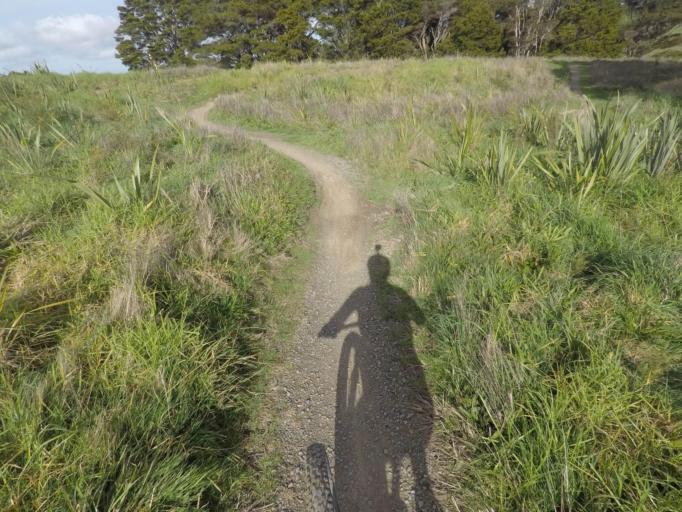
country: NZ
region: Auckland
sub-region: Auckland
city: Manukau City
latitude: -36.9960
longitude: 174.9125
